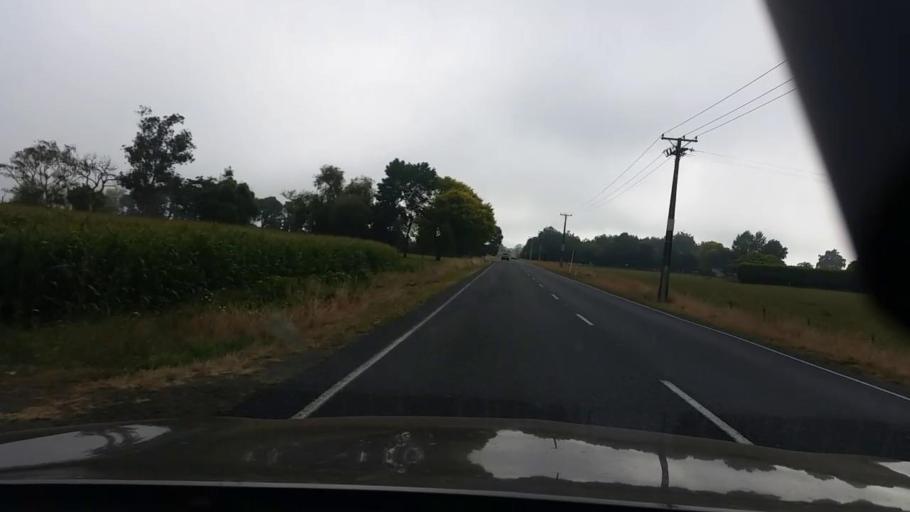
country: NZ
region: Waikato
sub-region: Hamilton City
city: Hamilton
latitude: -37.6252
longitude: 175.3237
